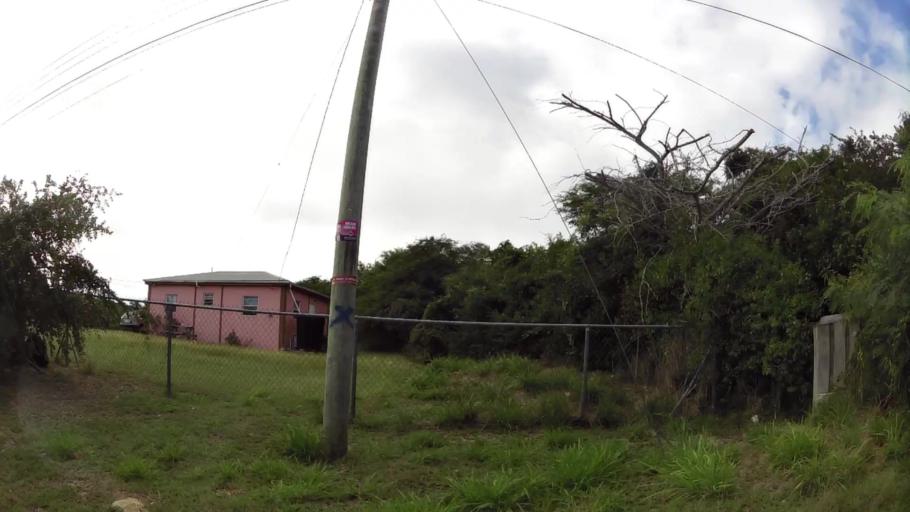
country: AG
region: Saint George
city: Piggotts
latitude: 17.1043
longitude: -61.8089
